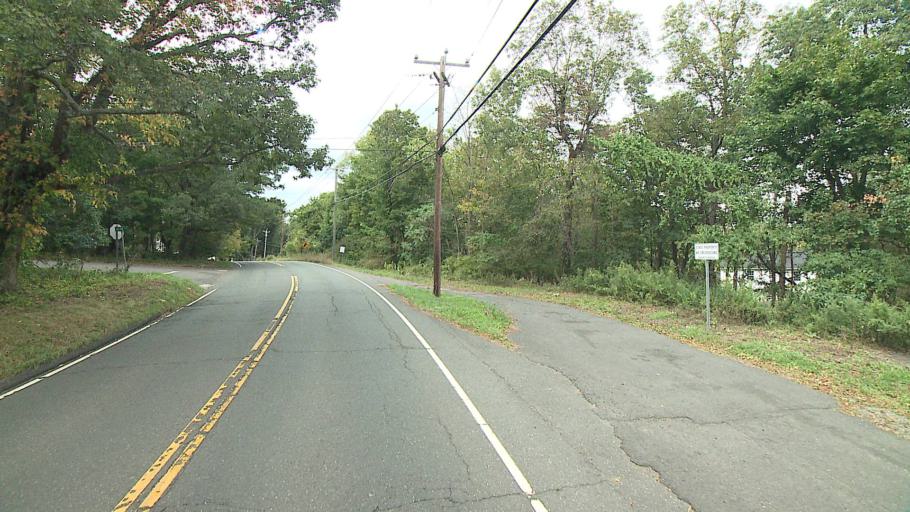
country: US
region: Connecticut
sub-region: Fairfield County
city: Ridgefield
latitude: 41.2586
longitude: -73.4920
